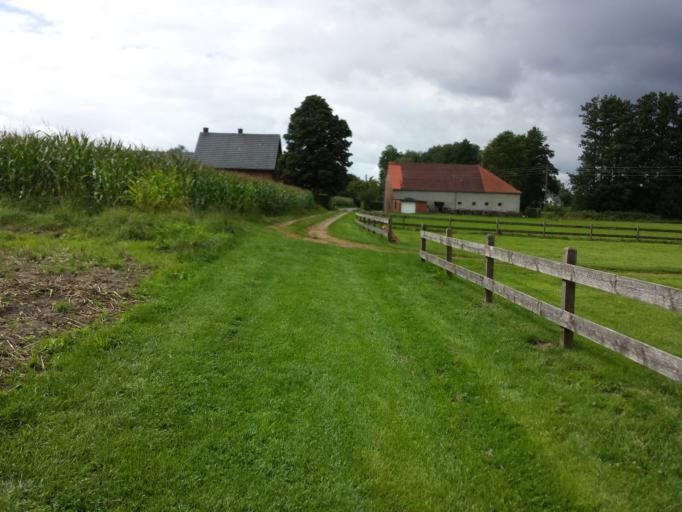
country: DE
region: North Rhine-Westphalia
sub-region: Regierungsbezirk Detmold
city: Guetersloh
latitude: 51.8862
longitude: 8.4035
